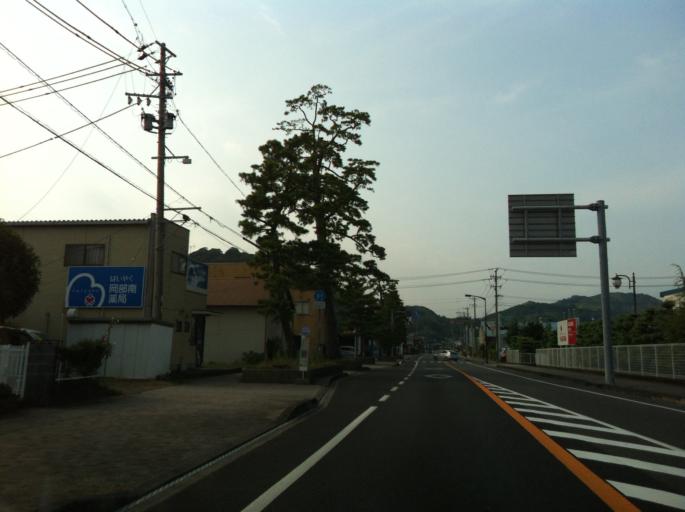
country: JP
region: Shizuoka
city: Fujieda
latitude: 34.9060
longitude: 138.2825
